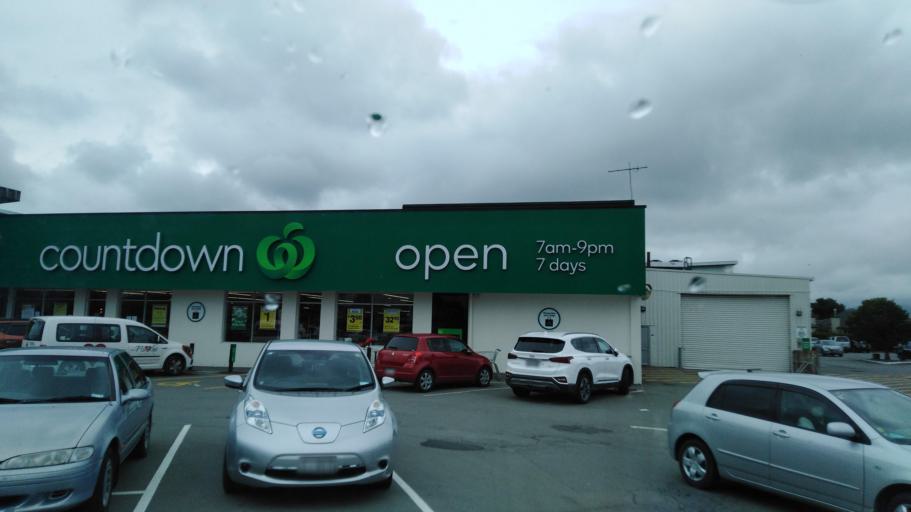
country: NZ
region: Marlborough
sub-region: Marlborough District
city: Blenheim
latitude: -41.5093
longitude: 173.9349
